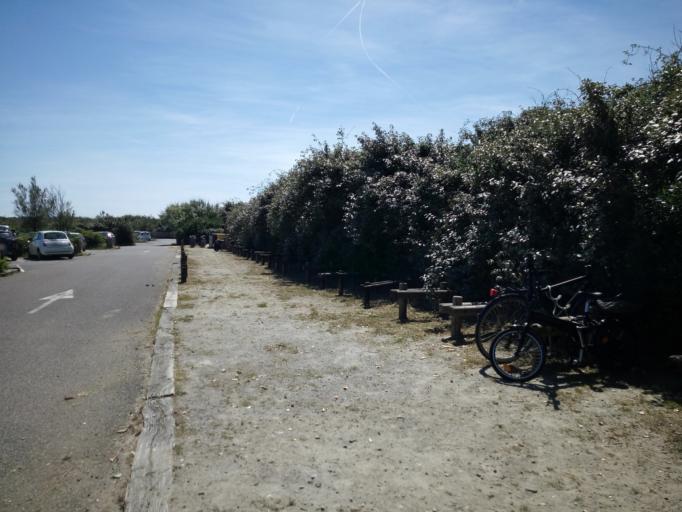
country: FR
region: Aquitaine
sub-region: Departement des Landes
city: Tarnos
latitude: 43.5584
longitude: -1.4985
